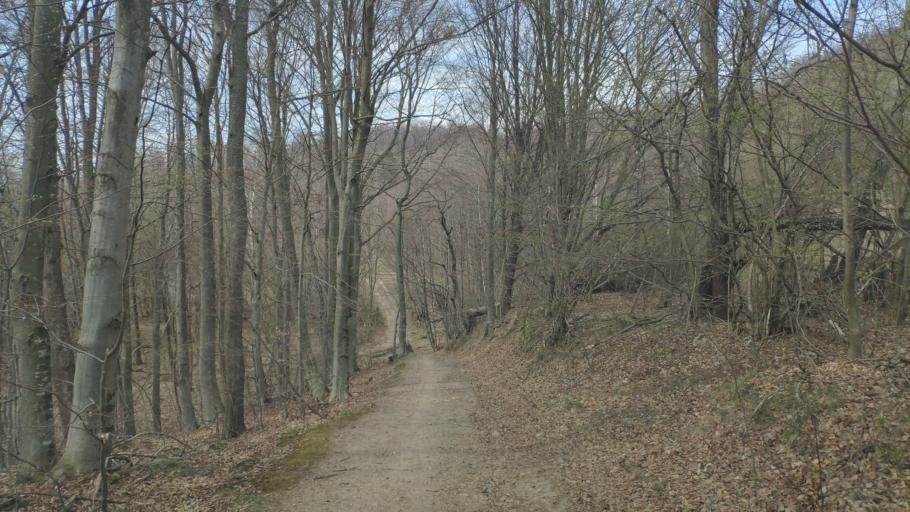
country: SK
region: Kosicky
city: Moldava nad Bodvou
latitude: 48.7479
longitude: 21.0242
